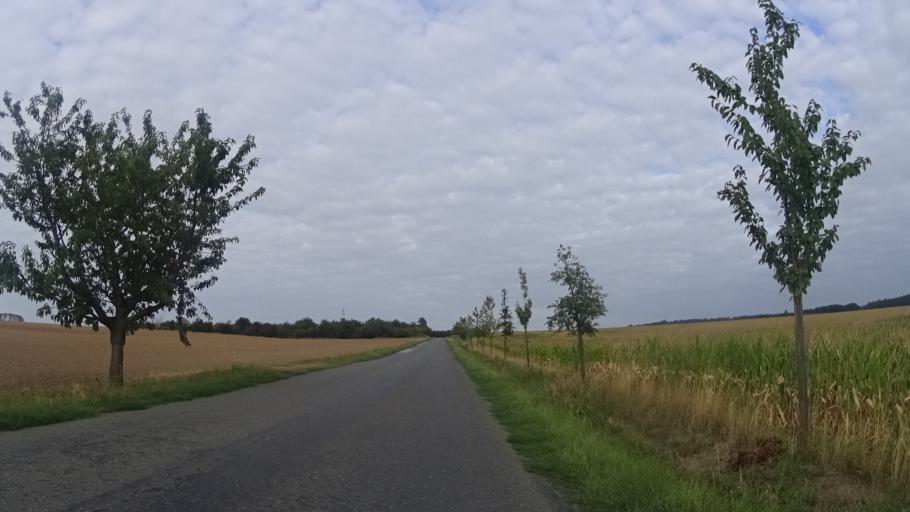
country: CZ
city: Stezery
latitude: 50.2126
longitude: 15.7409
